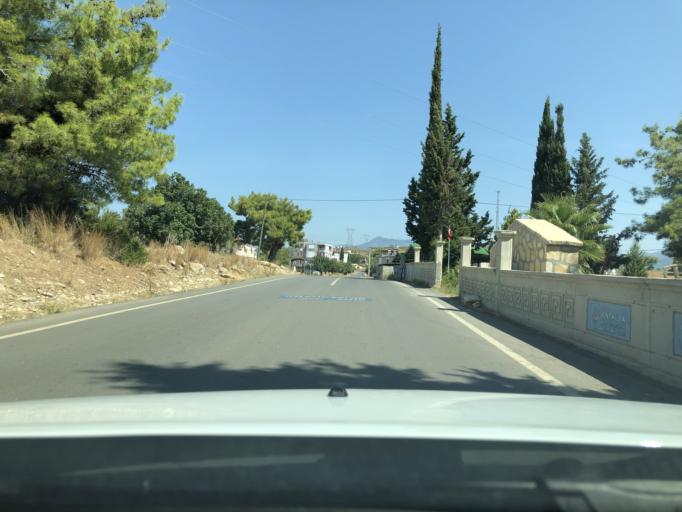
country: TR
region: Antalya
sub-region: Manavgat
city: Manavgat
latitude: 36.8169
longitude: 31.4888
